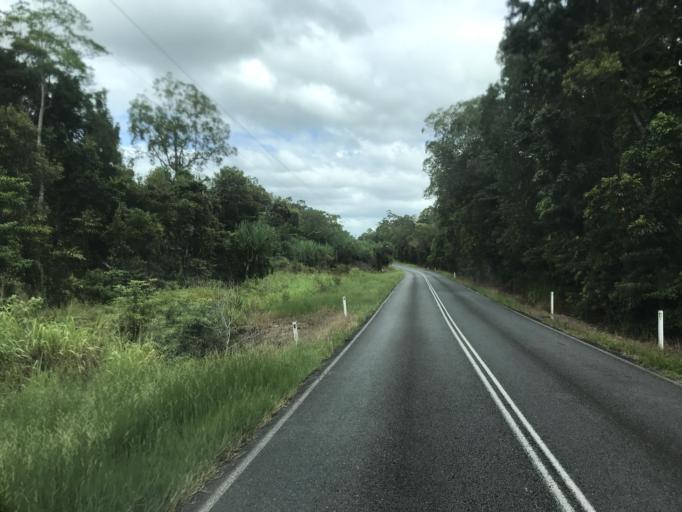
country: AU
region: Queensland
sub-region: Cassowary Coast
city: Innisfail
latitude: -17.8462
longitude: 146.0573
